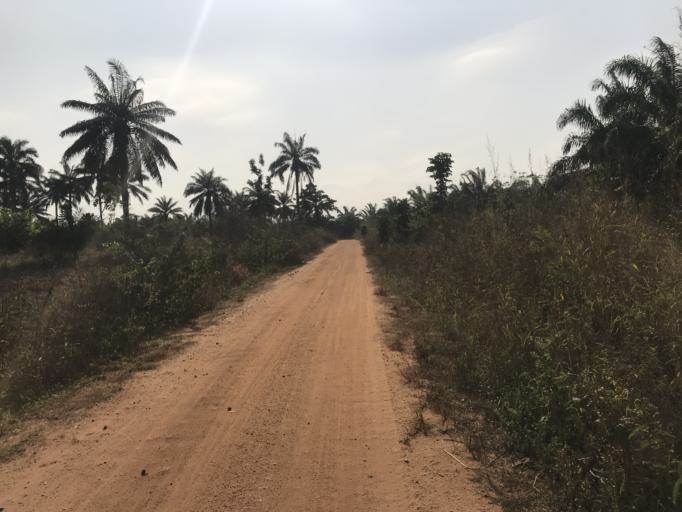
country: NG
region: Osun
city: Olupona
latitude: 7.6113
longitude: 4.1467
